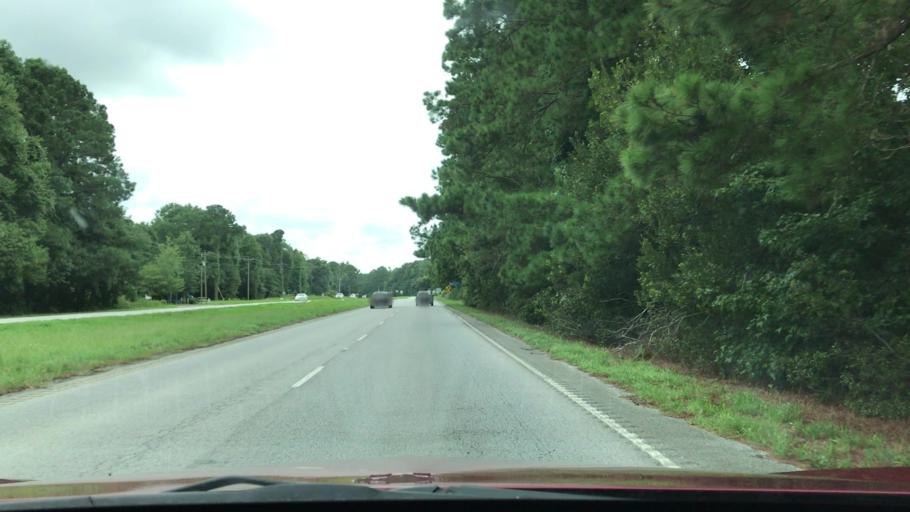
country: US
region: South Carolina
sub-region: Charleston County
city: Awendaw
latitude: 32.9414
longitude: -79.7079
